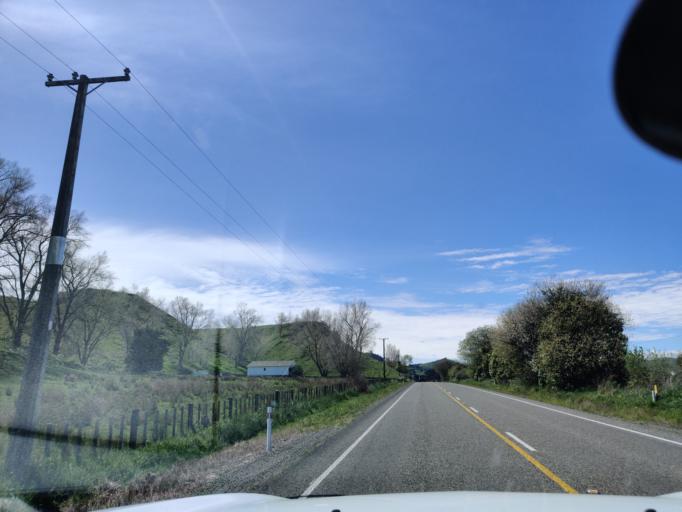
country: NZ
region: Manawatu-Wanganui
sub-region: Ruapehu District
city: Waiouru
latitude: -39.8529
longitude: 175.7294
